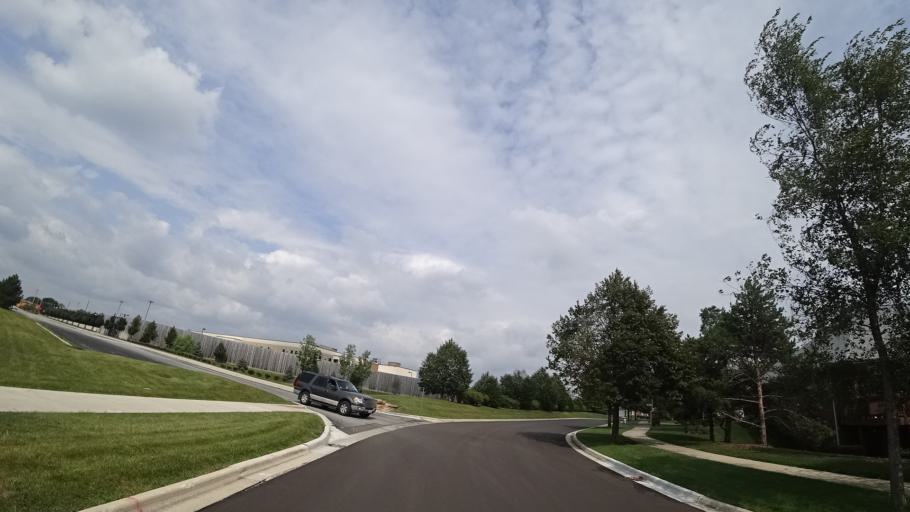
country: US
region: Illinois
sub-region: Cook County
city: Tinley Park
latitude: 41.5992
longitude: -87.7900
